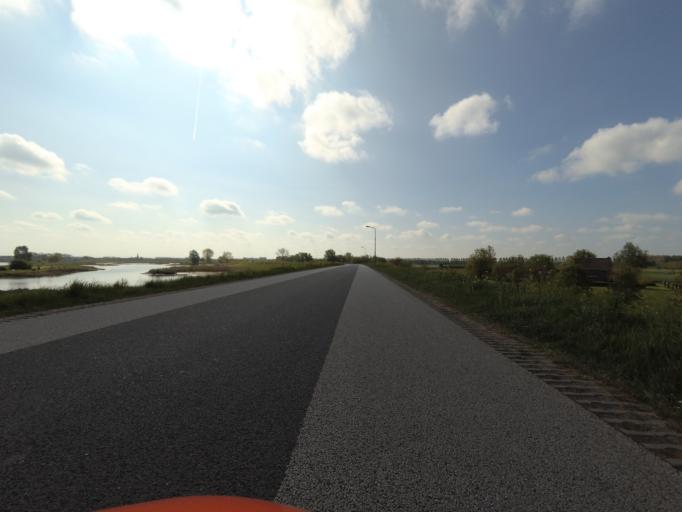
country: NL
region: Utrecht
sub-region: Gemeente IJsselstein
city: IJsselstein
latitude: 51.9692
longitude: 5.0153
